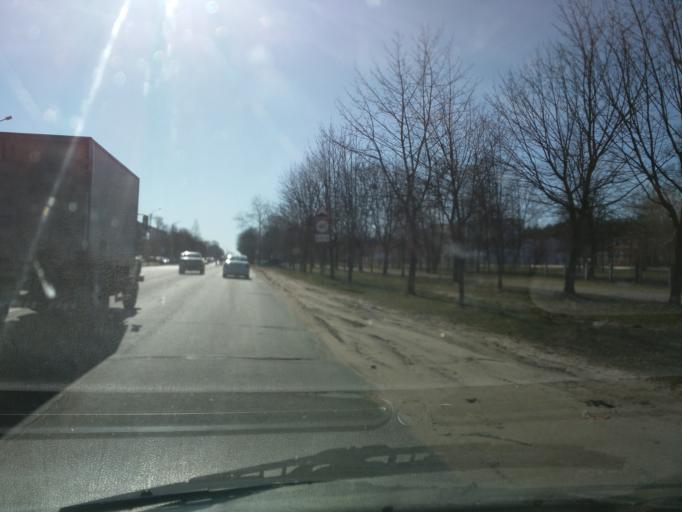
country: BY
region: Mogilev
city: Babruysk
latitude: 53.1746
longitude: 29.1868
